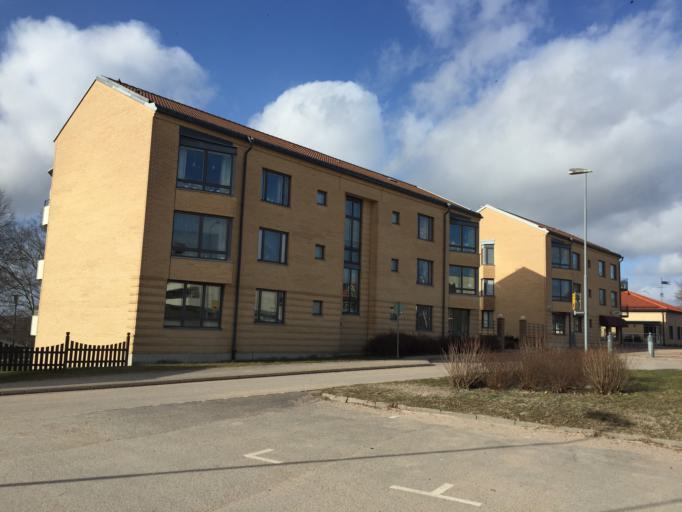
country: SE
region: Soedermanland
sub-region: Vingakers Kommun
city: Vingaker
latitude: 59.0424
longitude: 15.8710
